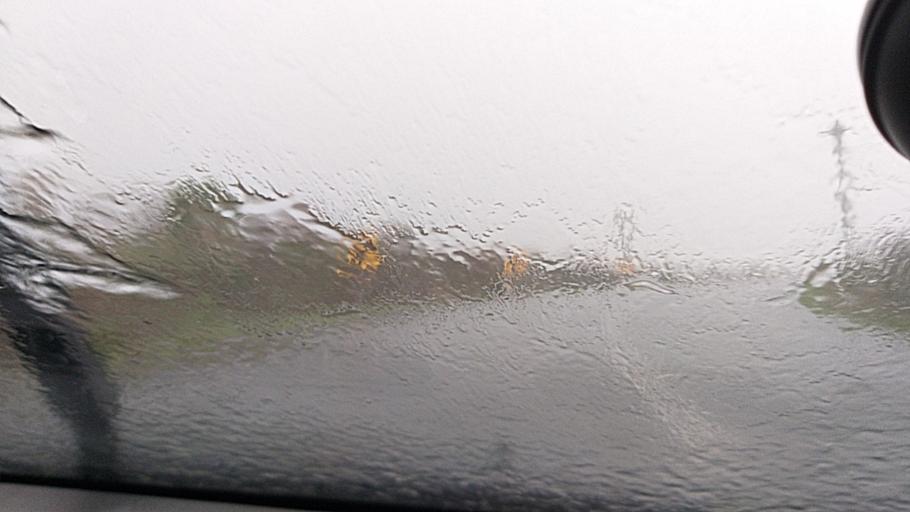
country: AU
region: New South Wales
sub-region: Wollondilly
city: Douglas Park
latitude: -34.1496
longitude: 150.7226
